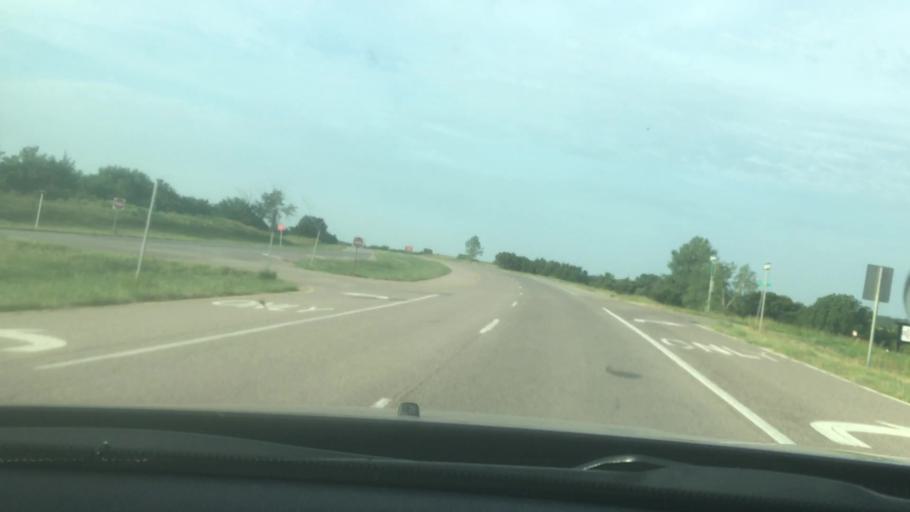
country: US
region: Oklahoma
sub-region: Pontotoc County
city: Ada
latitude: 34.7096
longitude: -96.7299
